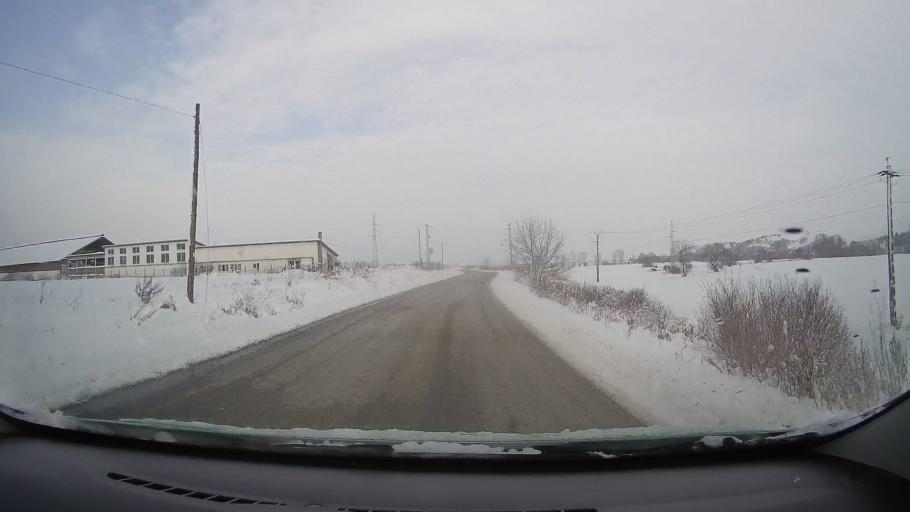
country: RO
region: Alba
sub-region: Comuna Pianu
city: Pianu de Jos
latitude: 45.9525
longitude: 23.4781
